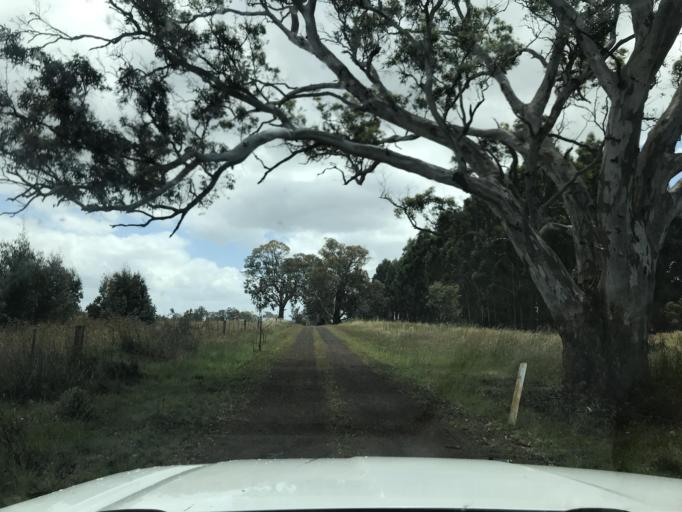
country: AU
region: South Australia
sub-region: Wattle Range
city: Penola
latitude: -37.2979
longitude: 141.4710
